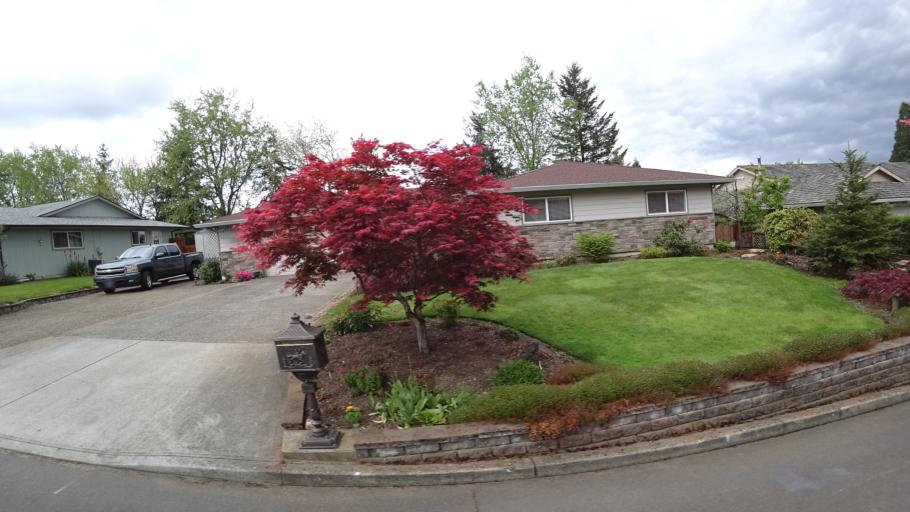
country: US
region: Oregon
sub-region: Washington County
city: Rockcreek
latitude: 45.5554
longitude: -122.8814
